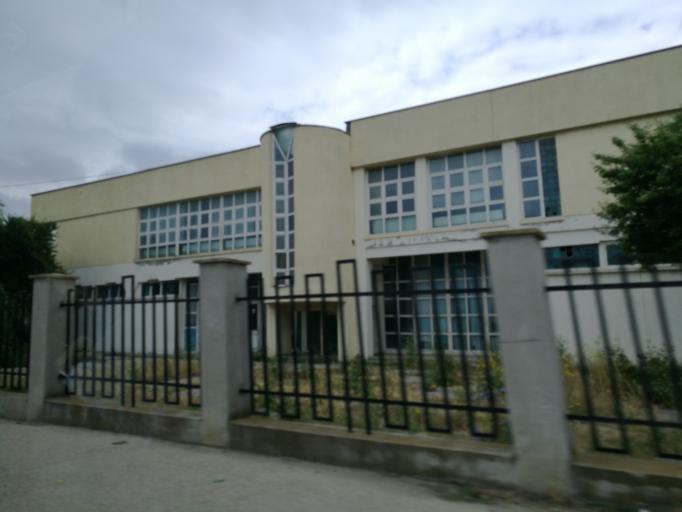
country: RO
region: Constanta
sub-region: Municipiul Mangalia
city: Mangalia
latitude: 43.8157
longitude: 28.5731
